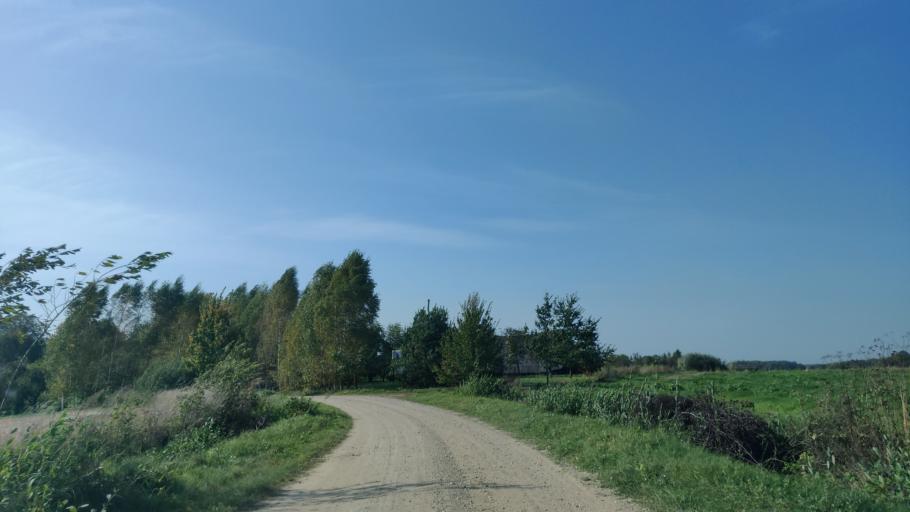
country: LT
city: Sirvintos
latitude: 54.9635
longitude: 24.7862
